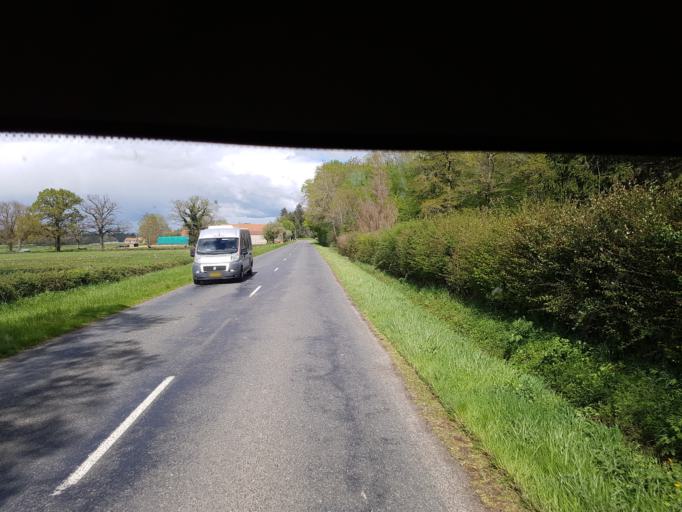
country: FR
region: Bourgogne
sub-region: Departement de Saone-et-Loire
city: Etang-sur-Arroux
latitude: 46.8084
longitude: 4.1574
